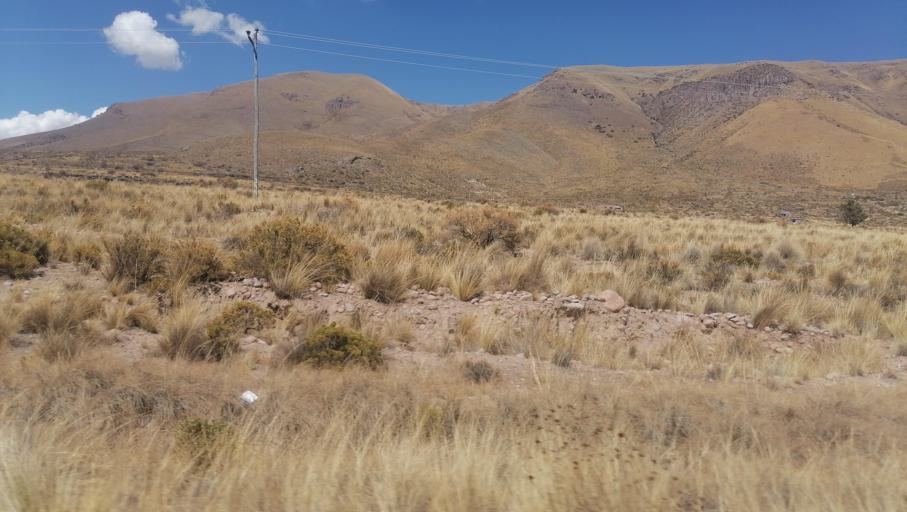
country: BO
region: Oruro
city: Challapata
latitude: -18.9794
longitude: -66.7805
